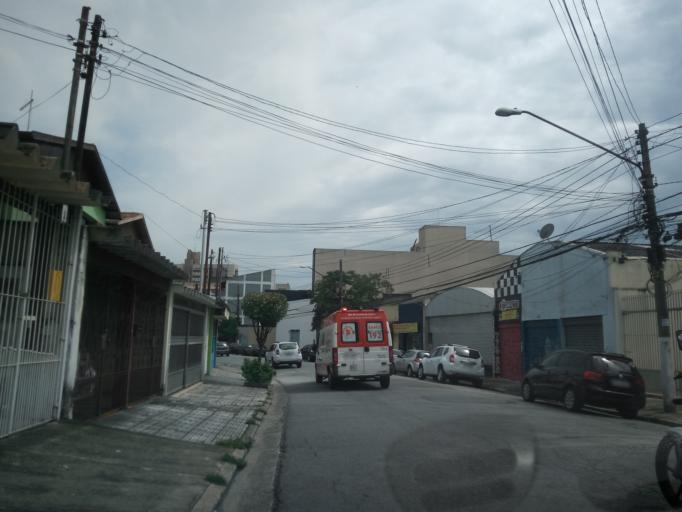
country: BR
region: Sao Paulo
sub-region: Sao Bernardo Do Campo
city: Sao Bernardo do Campo
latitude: -23.7166
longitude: -46.5526
